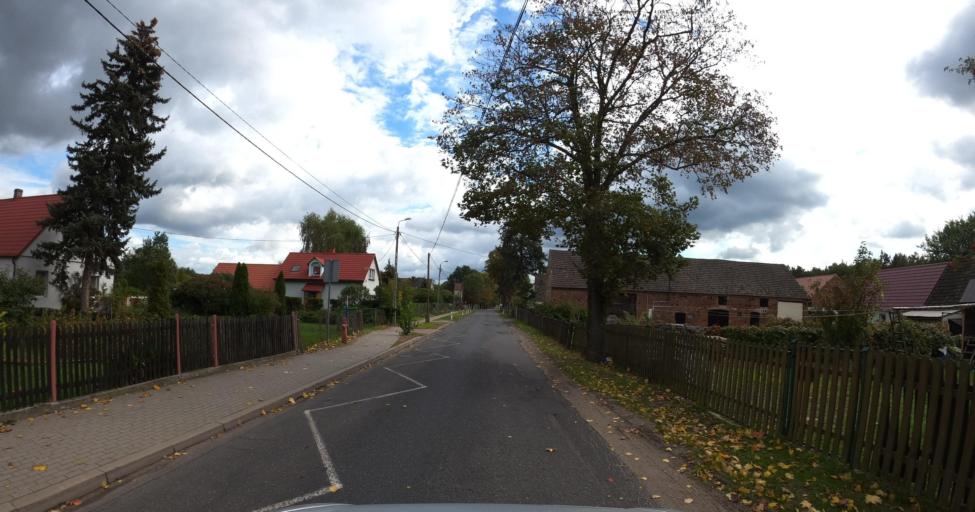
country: PL
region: Lubusz
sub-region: Zielona Gora
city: Zielona Gora
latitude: 51.9737
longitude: 15.6050
